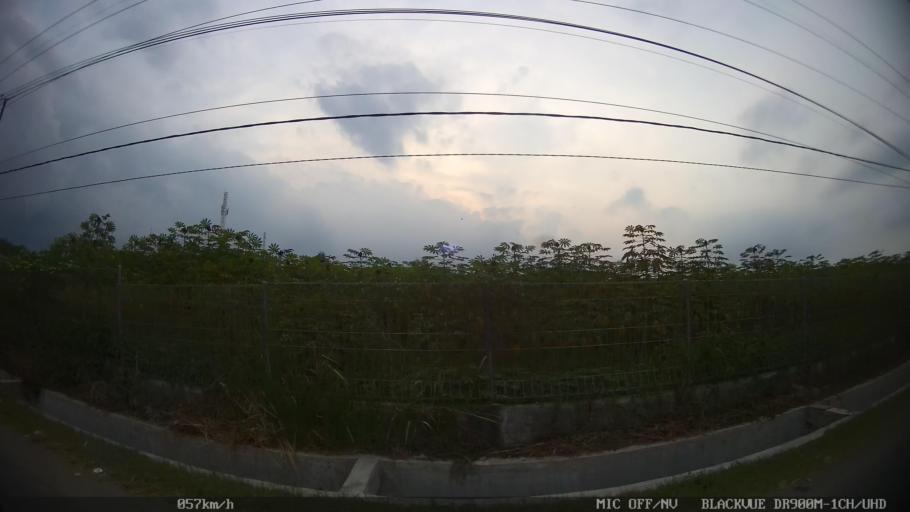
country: ID
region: North Sumatra
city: Sunggal
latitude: 3.5749
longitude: 98.6047
